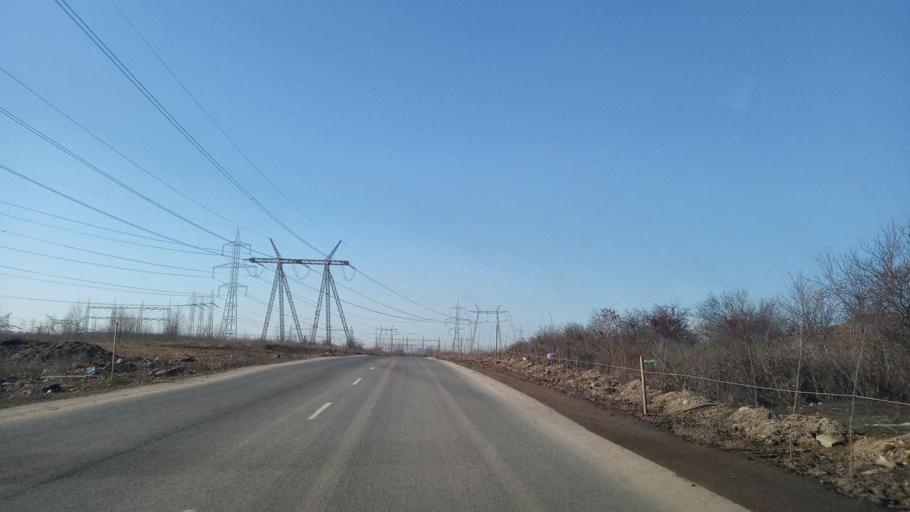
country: RO
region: Ilfov
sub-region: Comuna Popesti-Leordeni
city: Popesti-Leordeni
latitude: 44.3975
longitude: 26.1871
